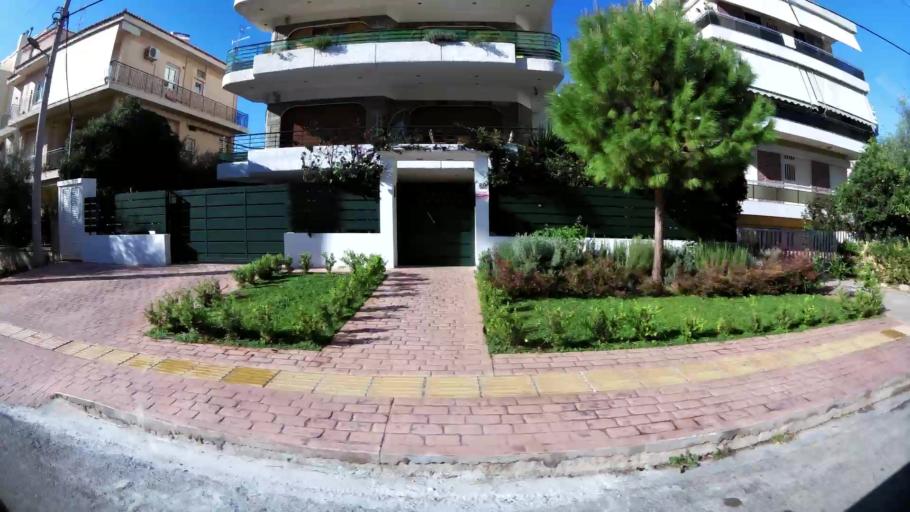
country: GR
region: Attica
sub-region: Nomarchia Athinas
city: Glyfada
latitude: 37.8597
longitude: 23.7670
